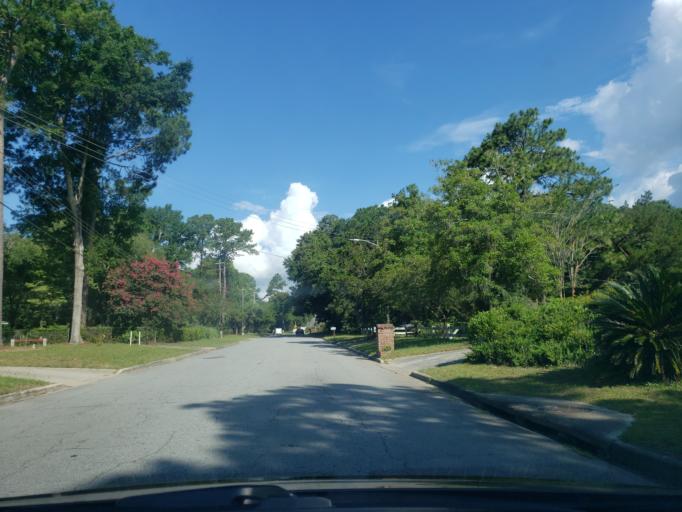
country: US
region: Georgia
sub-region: Chatham County
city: Montgomery
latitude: 31.9871
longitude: -81.1626
